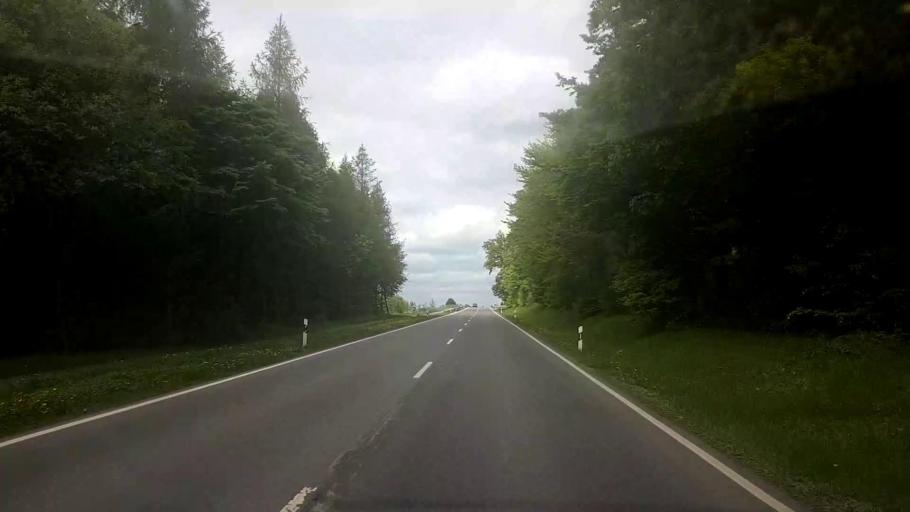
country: DE
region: Bavaria
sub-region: Upper Franconia
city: Lichtenfels
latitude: 50.1759
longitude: 11.0214
